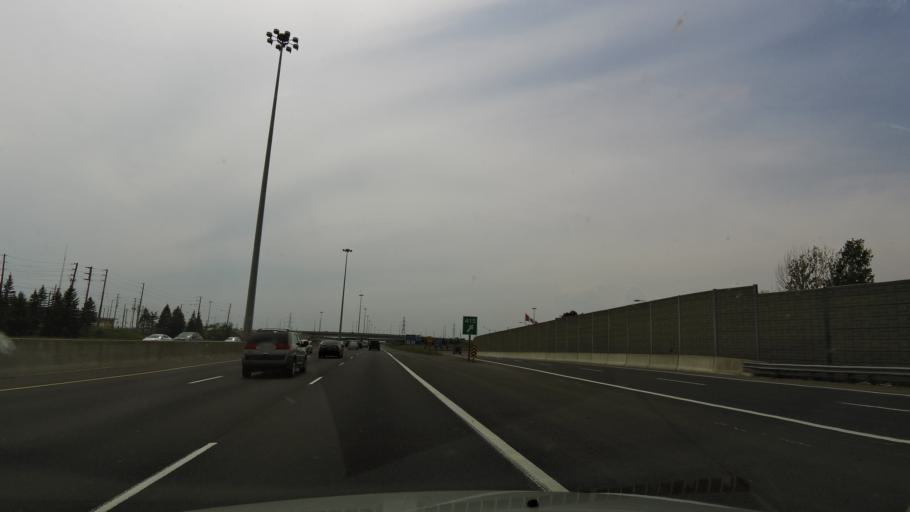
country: CA
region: Ontario
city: Oshawa
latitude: 43.8781
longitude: -78.8712
